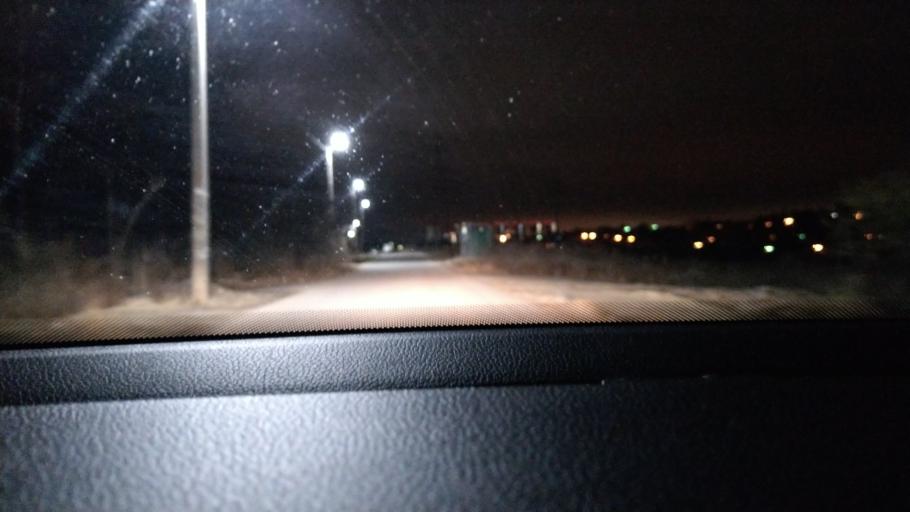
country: RU
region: Moskovskaya
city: Skhodnya
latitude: 55.9343
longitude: 37.2929
